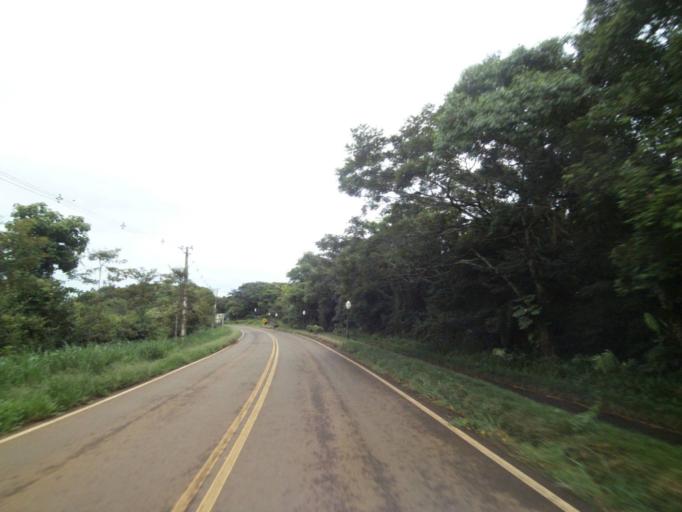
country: BR
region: Parana
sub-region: Guaraniacu
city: Guaraniacu
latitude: -25.0968
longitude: -52.8843
